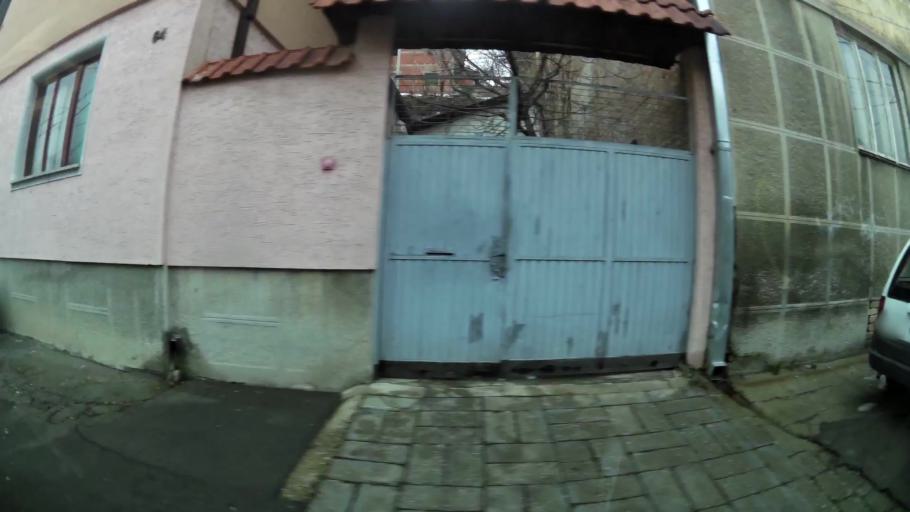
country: RS
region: Central Serbia
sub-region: Belgrade
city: Zemun
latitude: 44.8435
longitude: 20.4049
